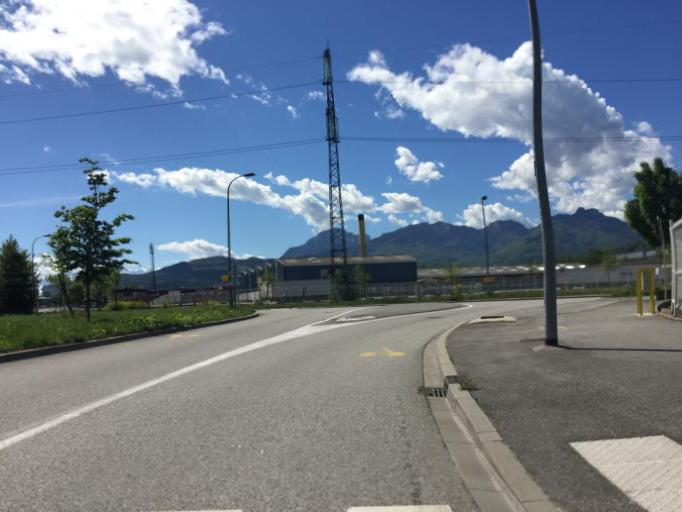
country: FR
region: Rhone-Alpes
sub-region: Departement de la Savoie
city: La Motte-Servolex
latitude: 45.5911
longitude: 5.8945
